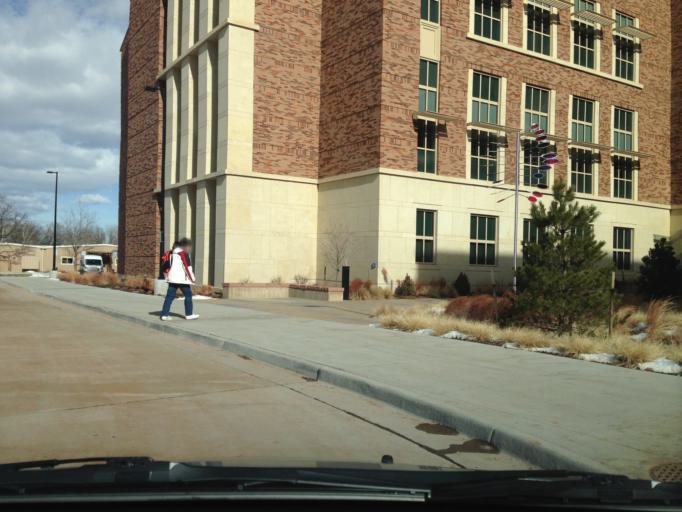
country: US
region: Colorado
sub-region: Boulder County
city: Boulder
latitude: 40.0089
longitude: -105.2495
